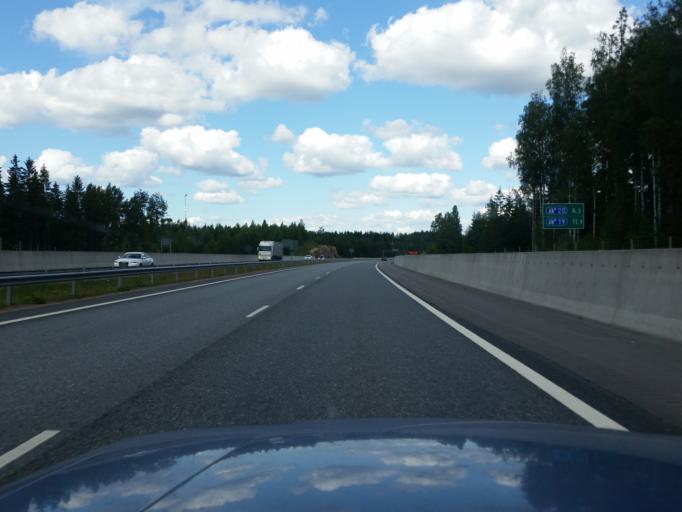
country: FI
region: Uusimaa
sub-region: Helsinki
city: Sammatti
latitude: 60.3474
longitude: 23.9021
